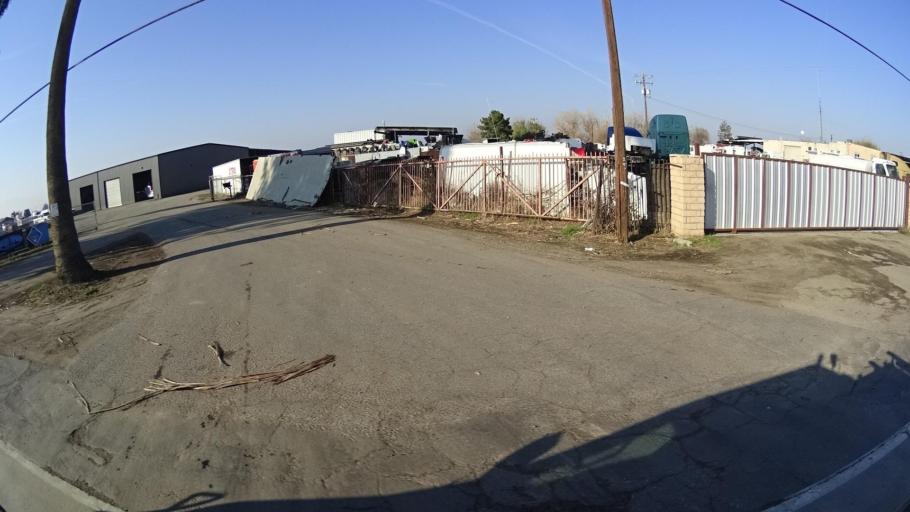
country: US
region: California
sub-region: Kern County
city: Greenfield
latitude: 35.2288
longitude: -119.0032
